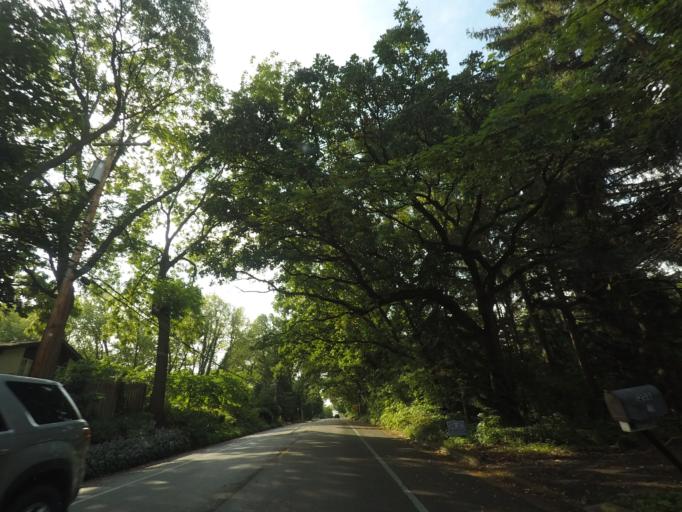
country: US
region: Wisconsin
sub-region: Dane County
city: Shorewood Hills
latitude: 43.0407
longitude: -89.4735
